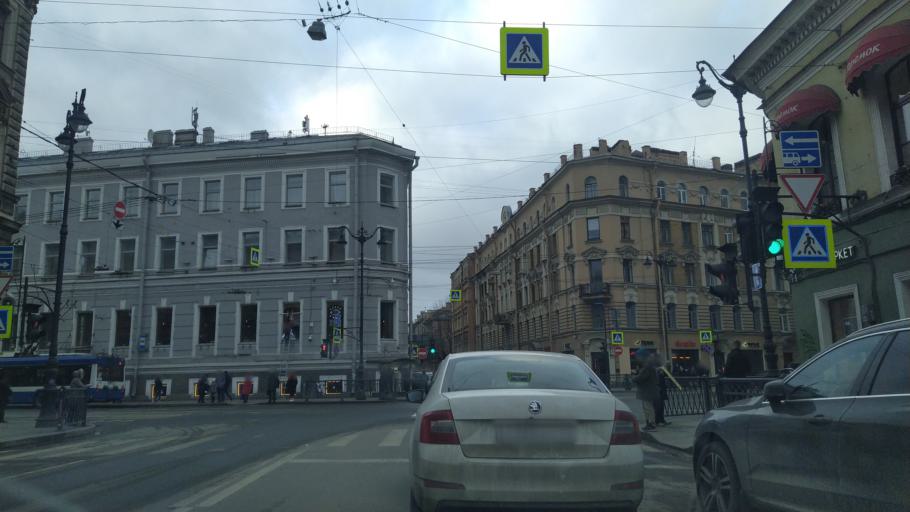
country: RU
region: St.-Petersburg
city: Centralniy
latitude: 59.9260
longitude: 30.3428
